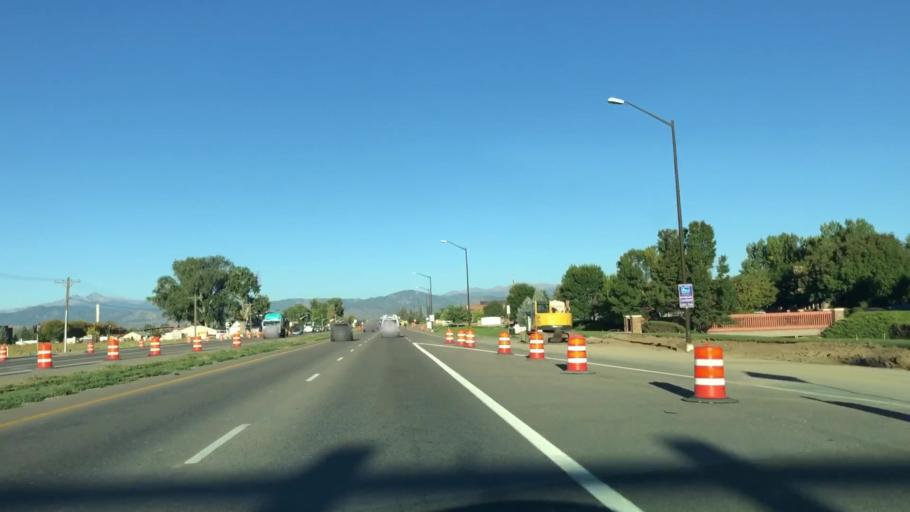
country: US
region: Colorado
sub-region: Larimer County
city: Loveland
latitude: 40.4062
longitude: -105.0216
